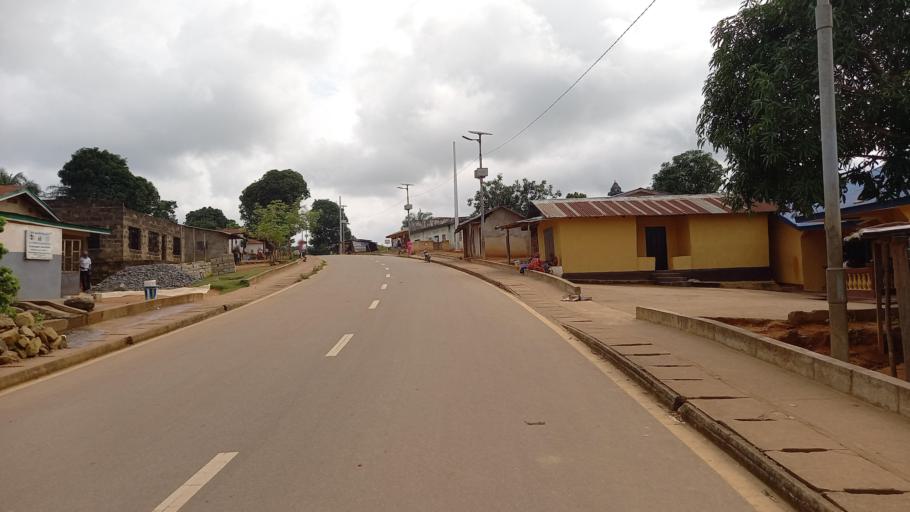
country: SL
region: Eastern Province
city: Kailahun
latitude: 8.2823
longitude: -10.5737
